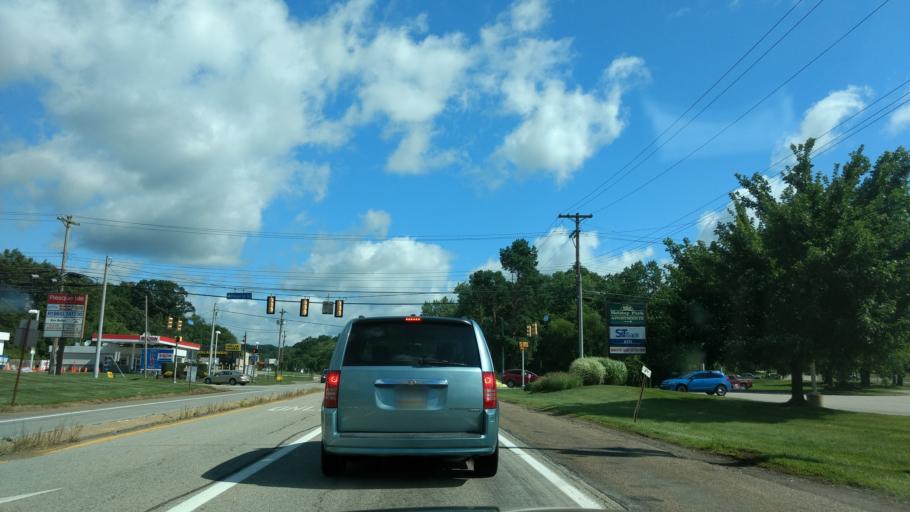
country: US
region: Pennsylvania
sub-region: Westmoreland County
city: Murrysville
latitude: 40.4630
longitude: -79.7056
